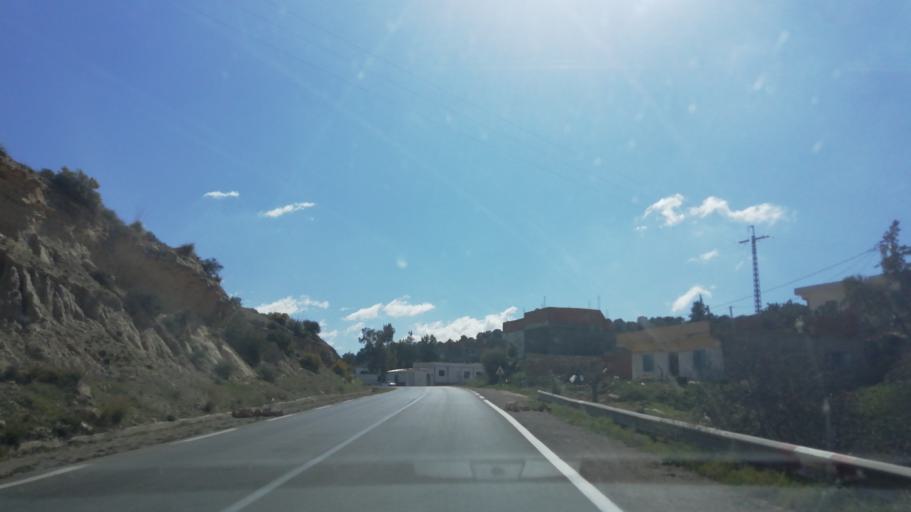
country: DZ
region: Mascara
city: Mascara
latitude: 35.4600
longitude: 0.1485
